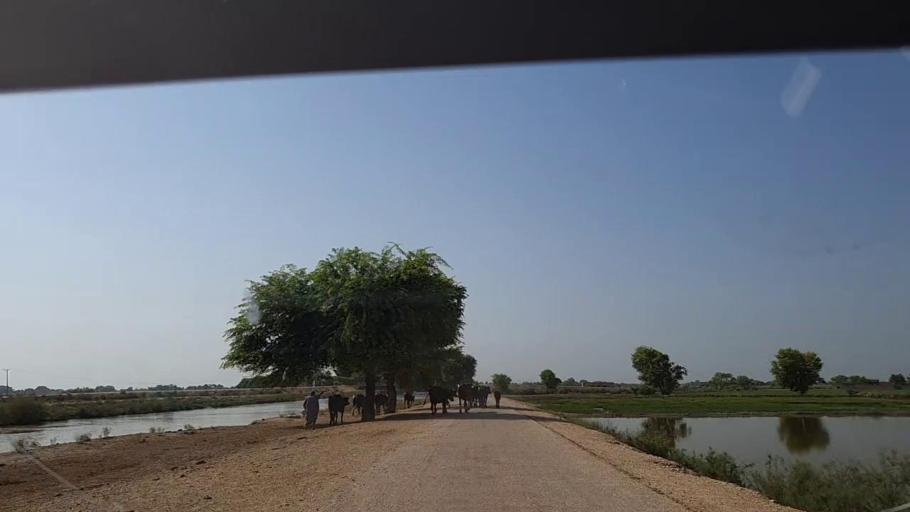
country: PK
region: Sindh
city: Ghauspur
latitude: 28.1991
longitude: 69.0433
